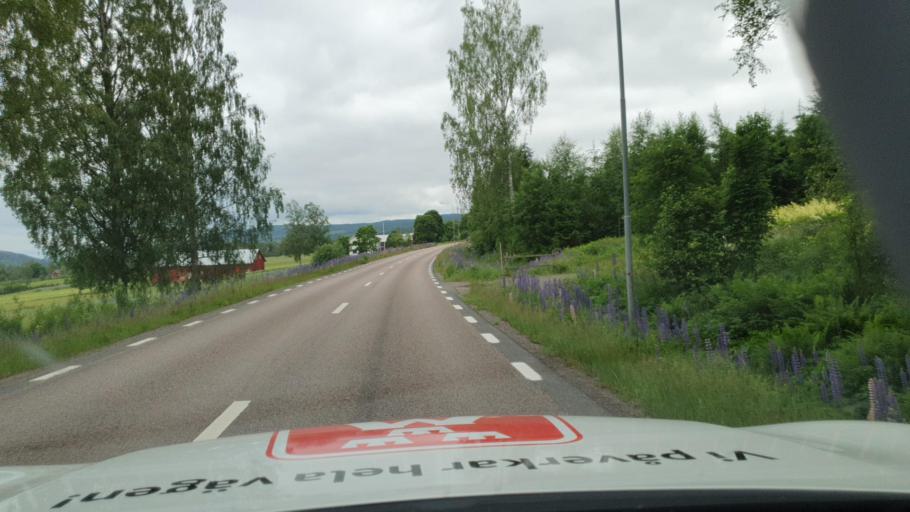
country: SE
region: Vaermland
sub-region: Sunne Kommun
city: Sunne
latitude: 59.8672
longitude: 12.9437
